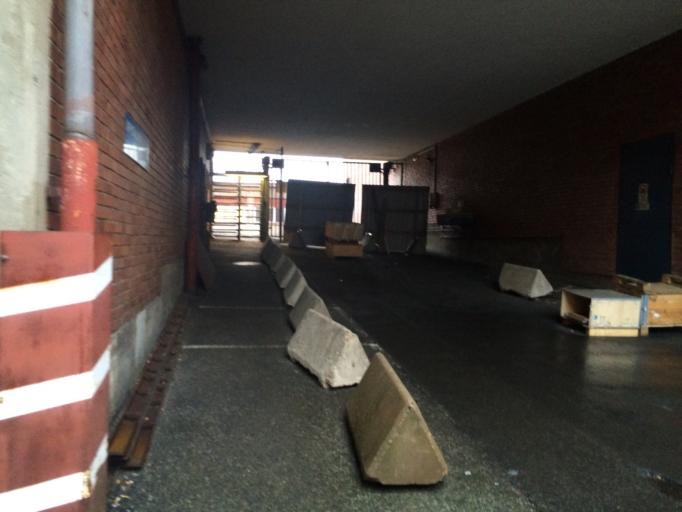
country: SE
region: Vaestra Goetaland
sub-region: Goteborg
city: Eriksbo
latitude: 57.7300
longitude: 12.0189
